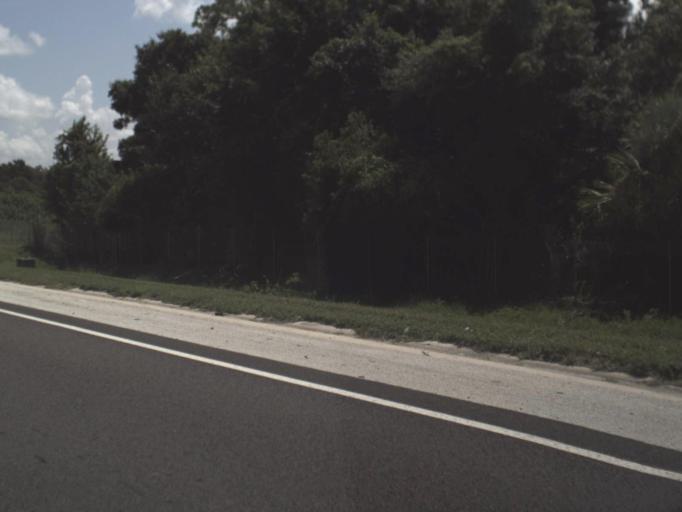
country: US
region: Florida
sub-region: Hillsborough County
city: East Lake-Orient Park
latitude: 27.9848
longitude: -82.3796
